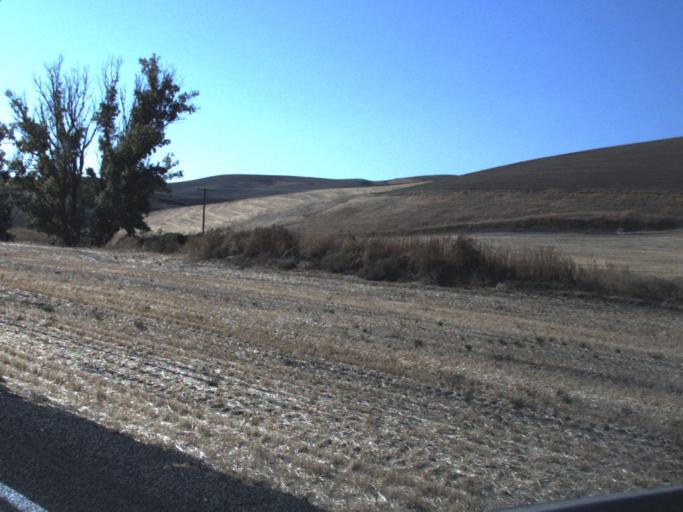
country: US
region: Washington
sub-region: Walla Walla County
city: Walla Walla
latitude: 46.2256
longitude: -118.3856
